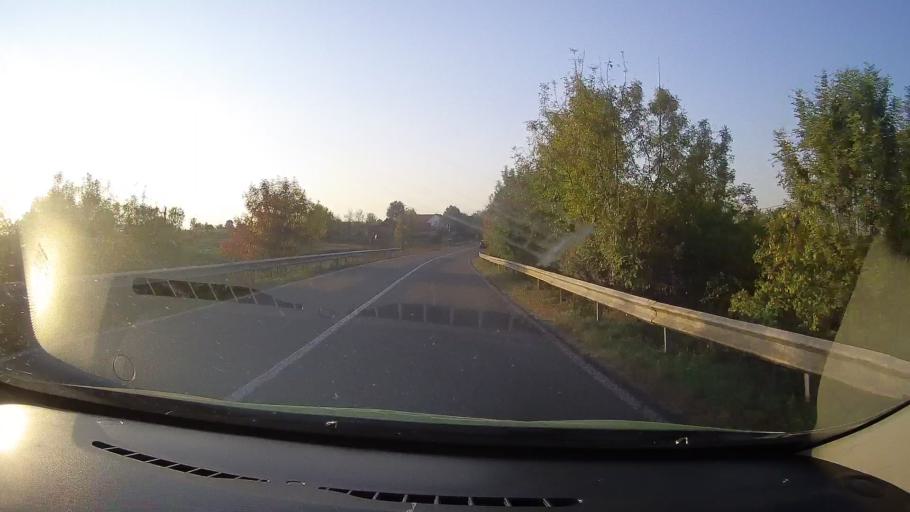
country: RO
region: Arad
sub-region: Comuna Barsa
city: Barsa
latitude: 46.3958
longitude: 22.0359
